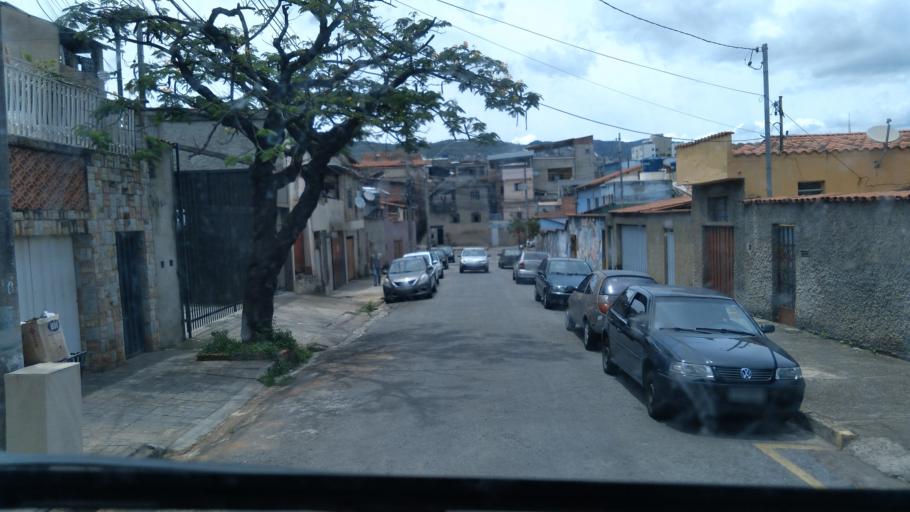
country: BR
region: Minas Gerais
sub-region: Belo Horizonte
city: Belo Horizonte
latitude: -19.9119
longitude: -43.9065
